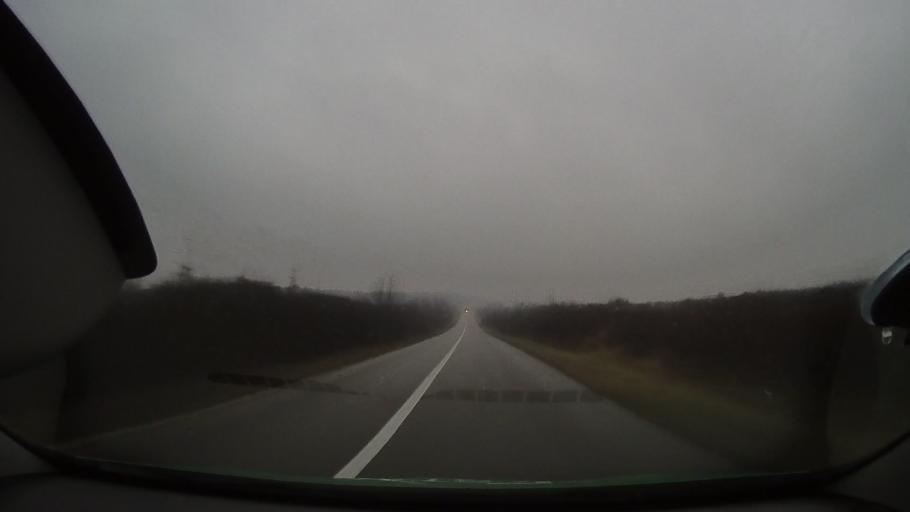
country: RO
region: Arad
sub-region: Comuna Craiova
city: Craiova
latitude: 46.5390
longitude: 21.9565
